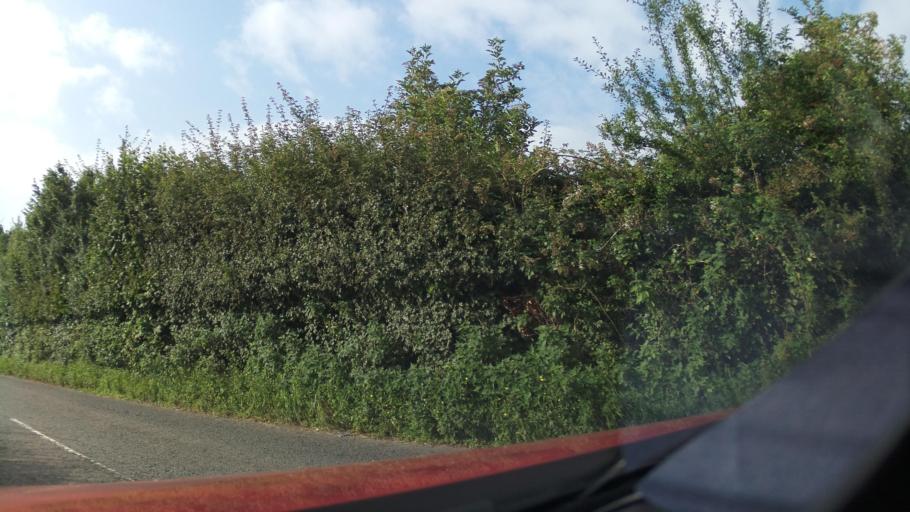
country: GB
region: England
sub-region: North Somerset
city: Winford
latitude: 51.3917
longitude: -2.6639
